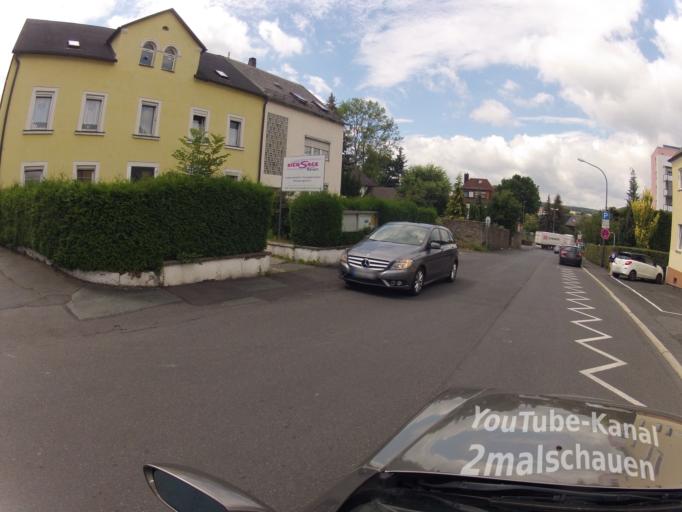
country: DE
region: Bavaria
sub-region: Upper Franconia
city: Marktredwitz
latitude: 49.9990
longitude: 12.0812
